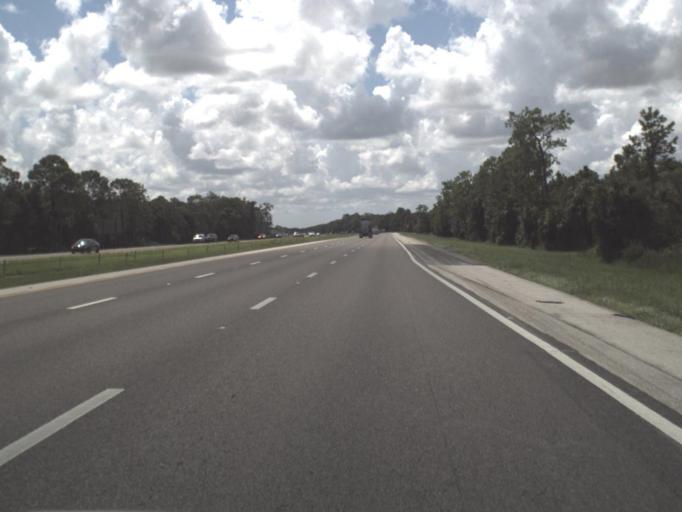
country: US
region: Florida
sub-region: Lee County
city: Bonita Springs
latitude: 26.3248
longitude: -81.7488
